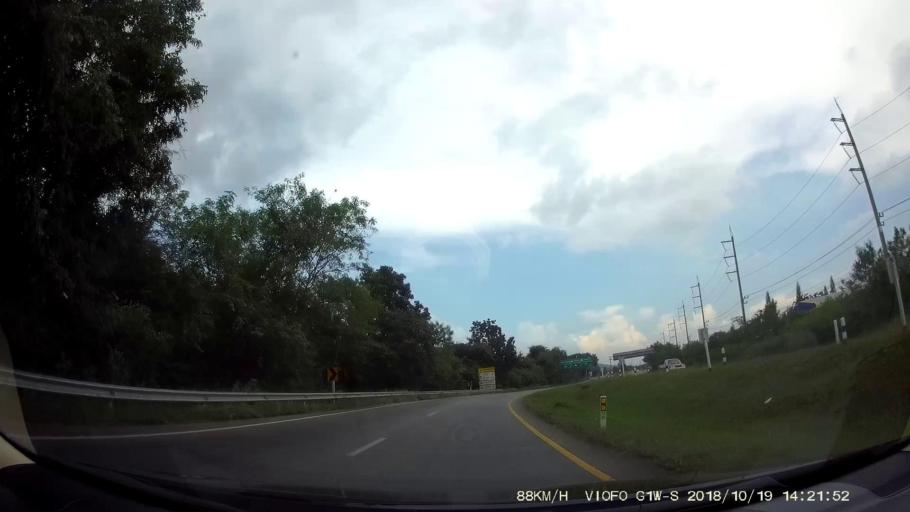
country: TH
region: Chaiyaphum
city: Kaeng Khro
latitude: 16.0571
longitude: 102.2705
